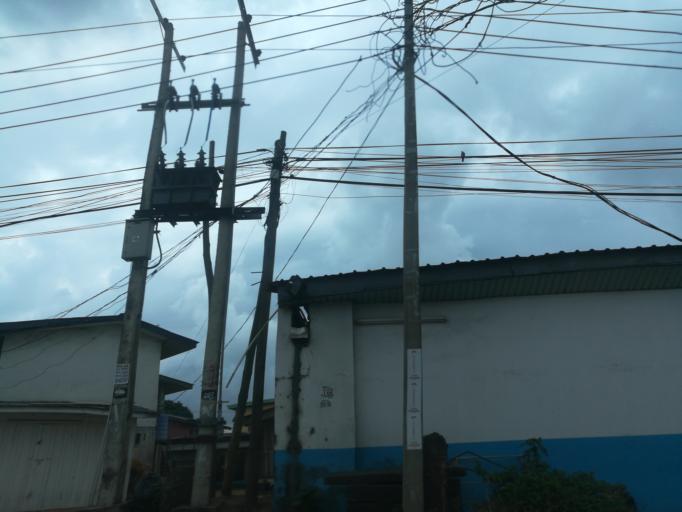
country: NG
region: Lagos
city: Ikeja
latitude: 6.6068
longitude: 3.3404
